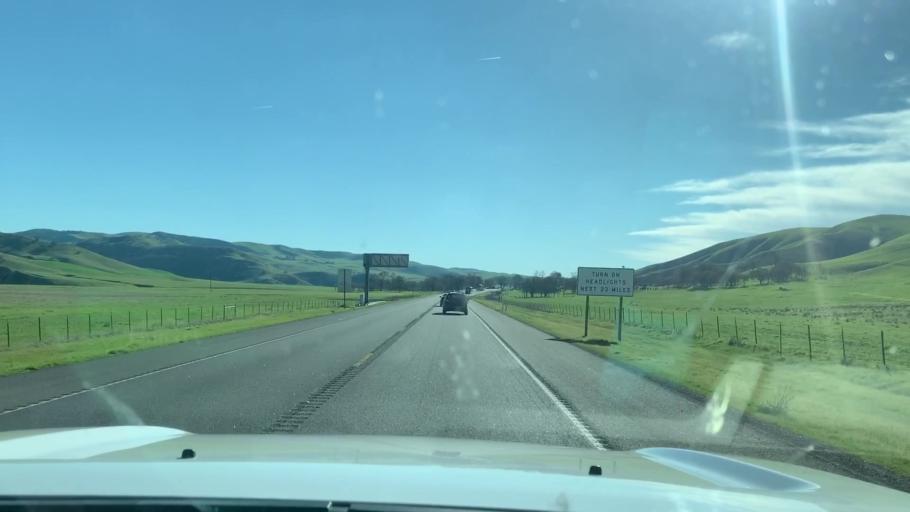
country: US
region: California
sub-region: San Luis Obispo County
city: Shandon
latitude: 35.7290
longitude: -120.2943
